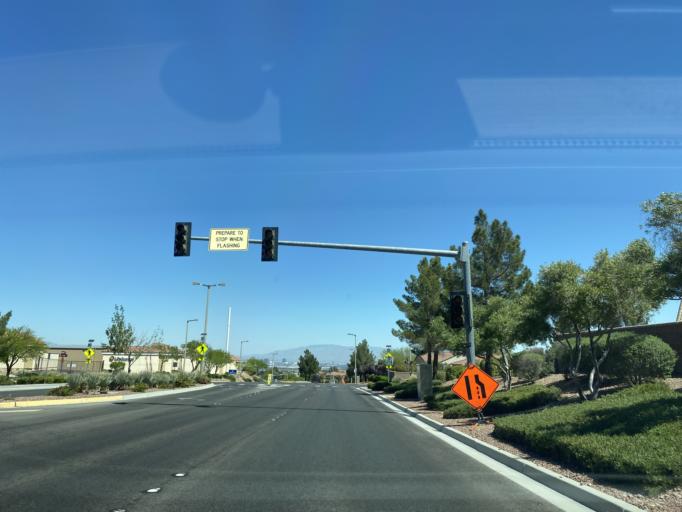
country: US
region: Nevada
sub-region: Clark County
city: Whitney
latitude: 35.9514
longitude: -115.0922
